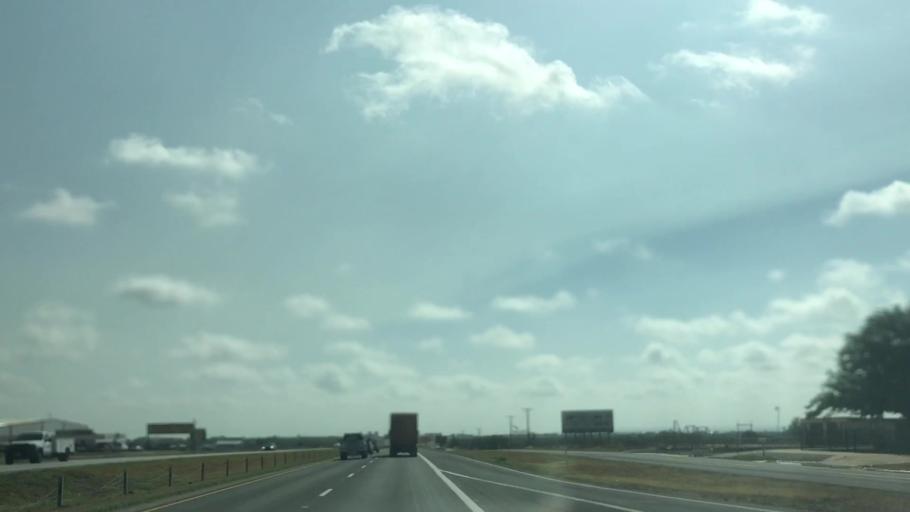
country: US
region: Texas
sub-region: Nolan County
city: Roscoe
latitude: 32.4506
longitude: -100.4829
